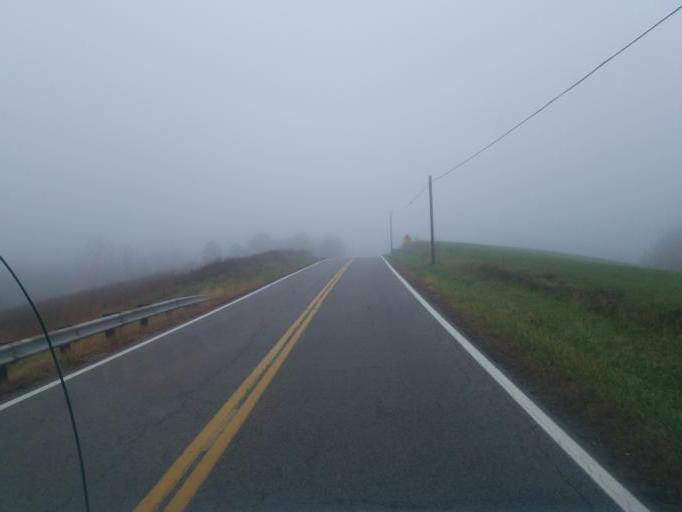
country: US
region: Ohio
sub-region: Morgan County
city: McConnelsville
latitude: 39.6081
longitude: -81.8737
